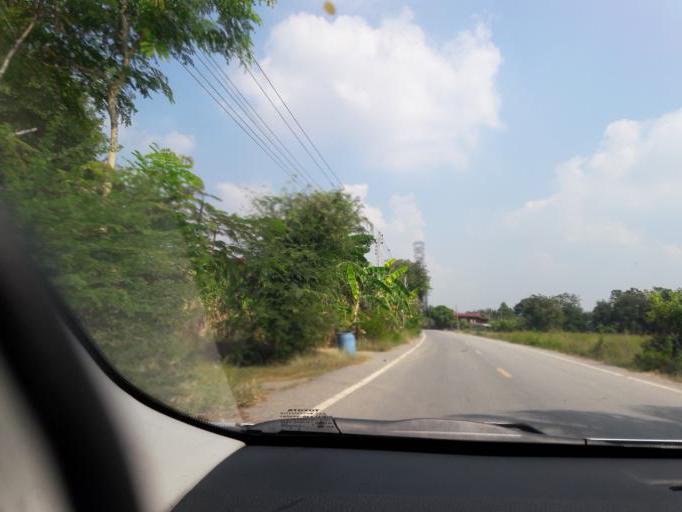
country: TH
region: Ang Thong
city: Ang Thong
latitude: 14.5694
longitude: 100.4108
